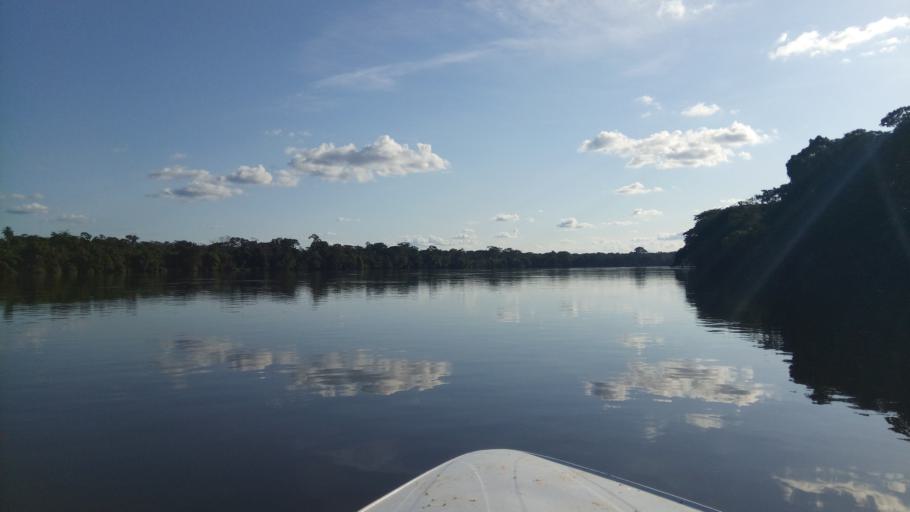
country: CD
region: Eastern Province
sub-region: Sous-Region de la Tshopo
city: Yangambi
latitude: 0.2352
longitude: 24.1065
